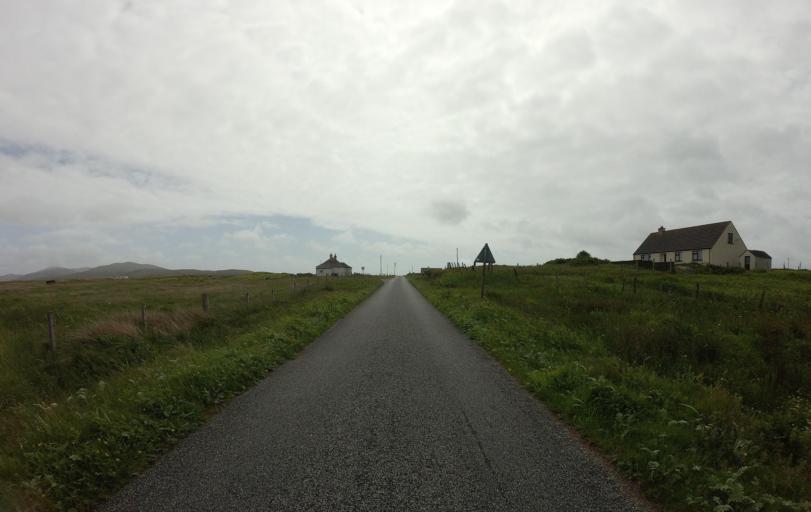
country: GB
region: Scotland
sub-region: Eilean Siar
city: Isle of South Uist
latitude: 57.2492
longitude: -7.4043
